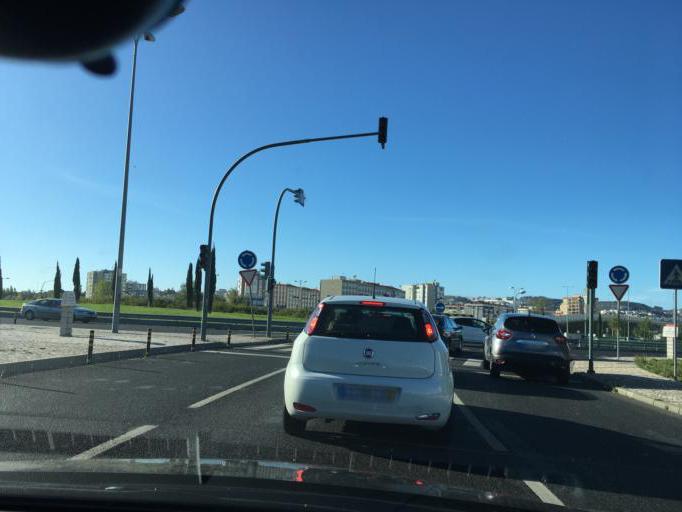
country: PT
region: Lisbon
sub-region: Odivelas
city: Pontinha
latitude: 38.7597
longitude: -9.1997
